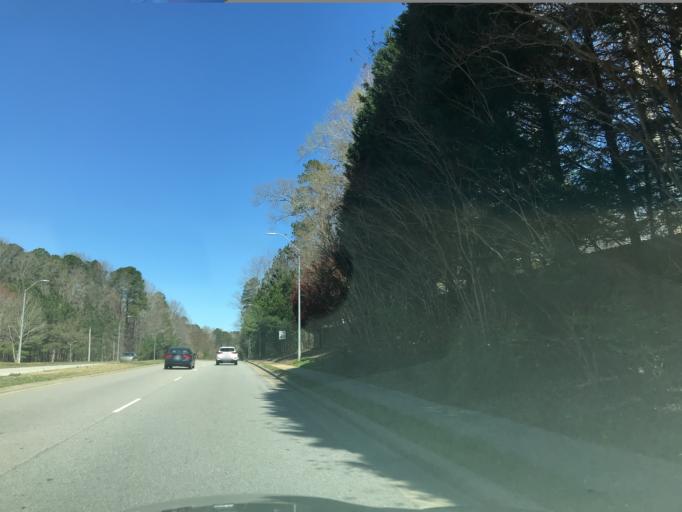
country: US
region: North Carolina
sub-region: Wake County
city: Garner
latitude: 35.7042
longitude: -78.6408
